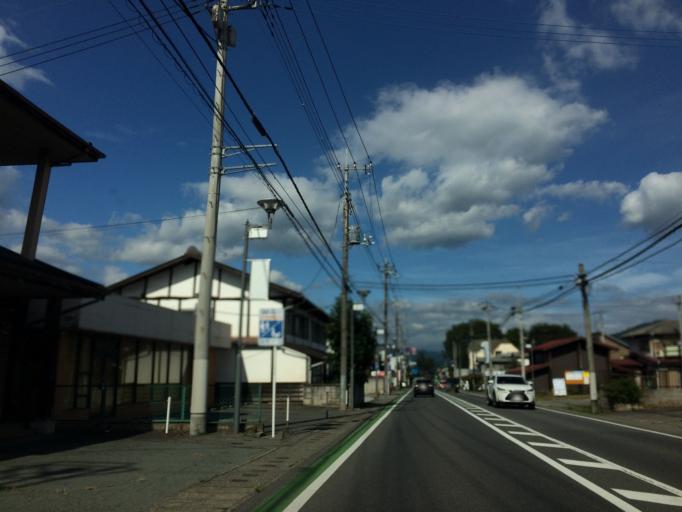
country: JP
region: Gunma
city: Nakanojomachi
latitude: 36.5730
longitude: 138.8292
